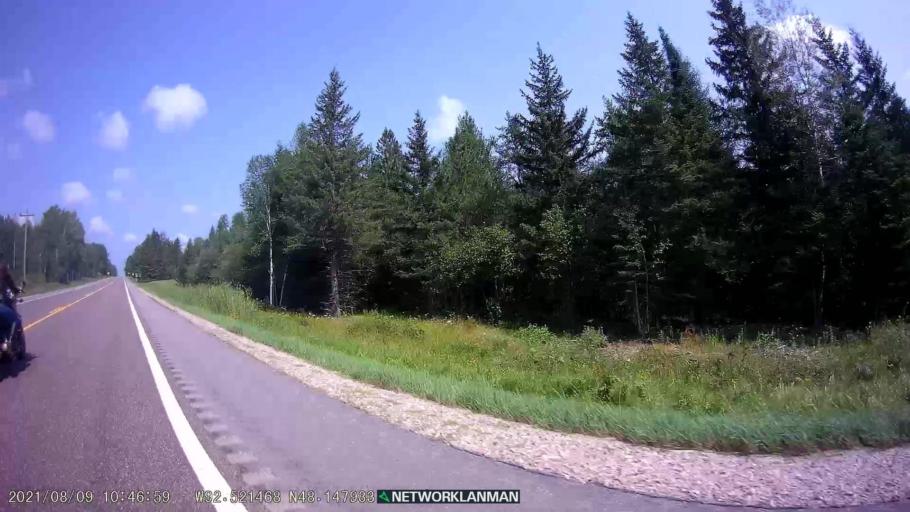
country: US
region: Minnesota
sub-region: Saint Louis County
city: Parkville
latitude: 48.1479
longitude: -92.5211
